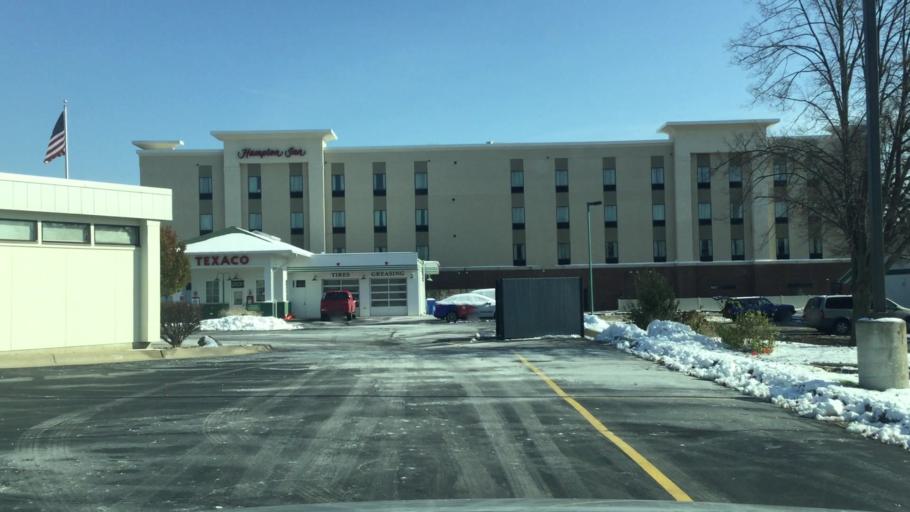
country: US
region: Michigan
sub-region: Kalamazoo County
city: Portage
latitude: 42.2414
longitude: -85.5596
